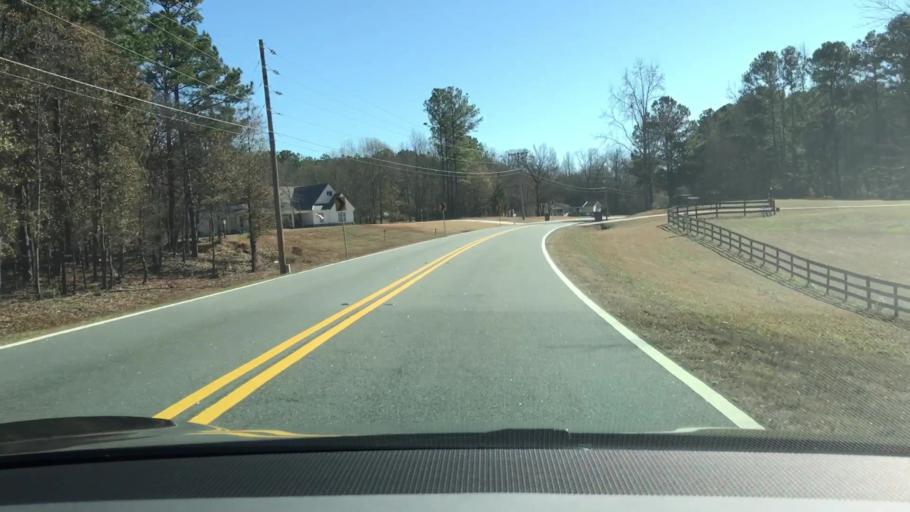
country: US
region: Georgia
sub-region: Walton County
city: Monroe
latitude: 33.8579
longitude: -83.7382
